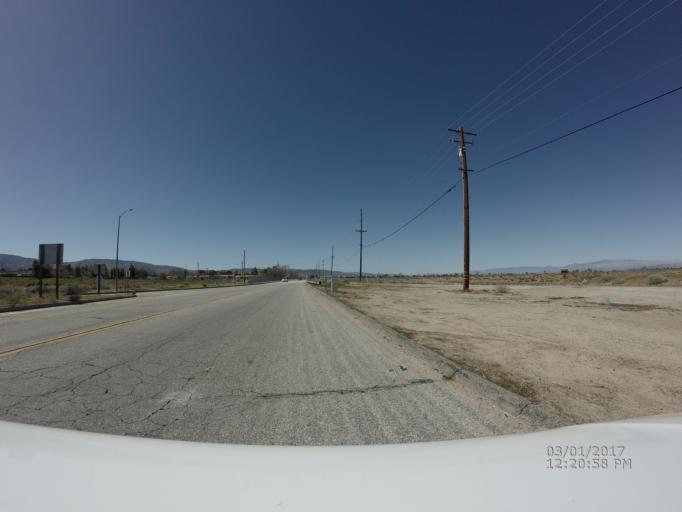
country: US
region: California
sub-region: Los Angeles County
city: Desert View Highlands
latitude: 34.6312
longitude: -118.1519
